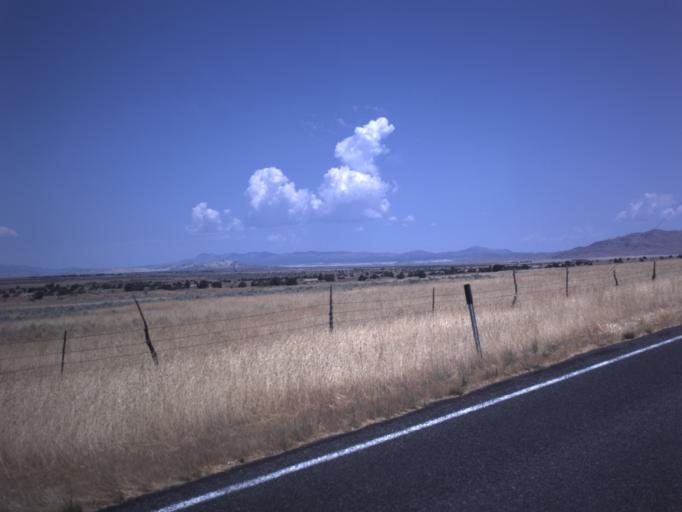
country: US
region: Utah
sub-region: Millard County
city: Delta
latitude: 39.4339
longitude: -112.3216
